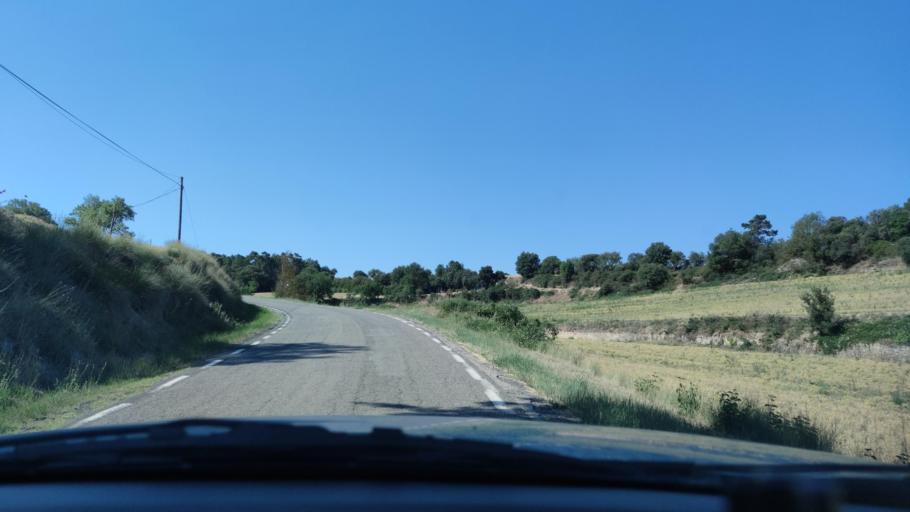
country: ES
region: Catalonia
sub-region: Provincia de Lleida
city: Sant Guim de Freixenet
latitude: 41.6730
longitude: 1.4063
